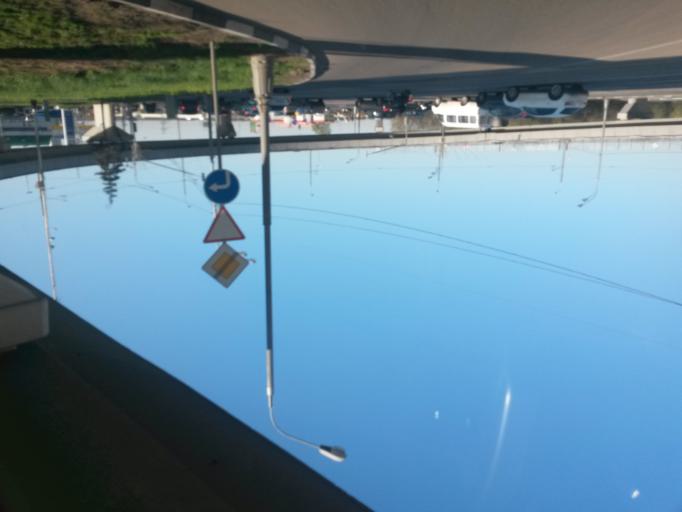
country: RU
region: Moscow
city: Annino
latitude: 55.5794
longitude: 37.5958
